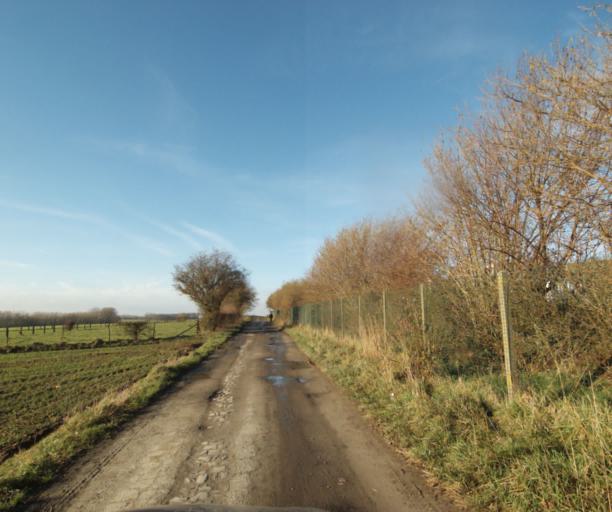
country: FR
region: Nord-Pas-de-Calais
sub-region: Departement du Nord
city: Curgies
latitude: 50.3159
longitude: 3.6017
